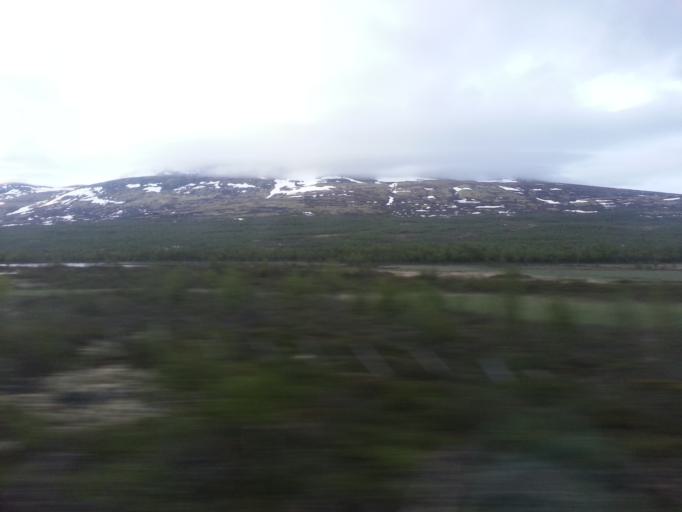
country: NO
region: Oppland
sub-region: Dovre
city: Dovre
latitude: 62.1446
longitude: 9.3120
